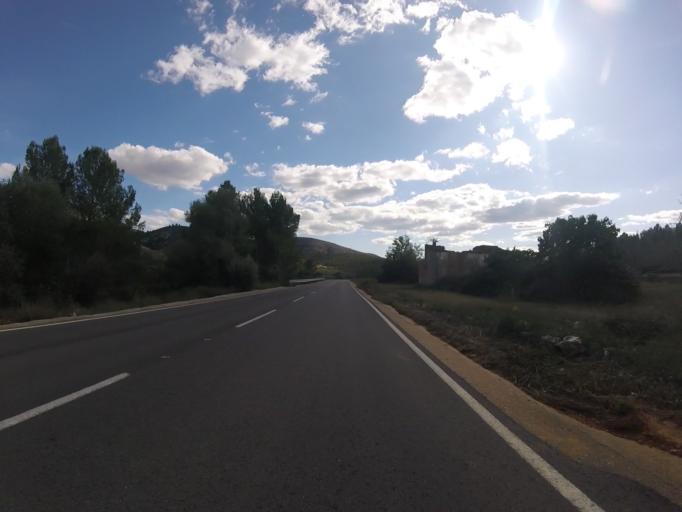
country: ES
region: Valencia
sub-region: Provincia de Castello
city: Cuevas de Vinroma
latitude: 40.3028
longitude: 0.1648
